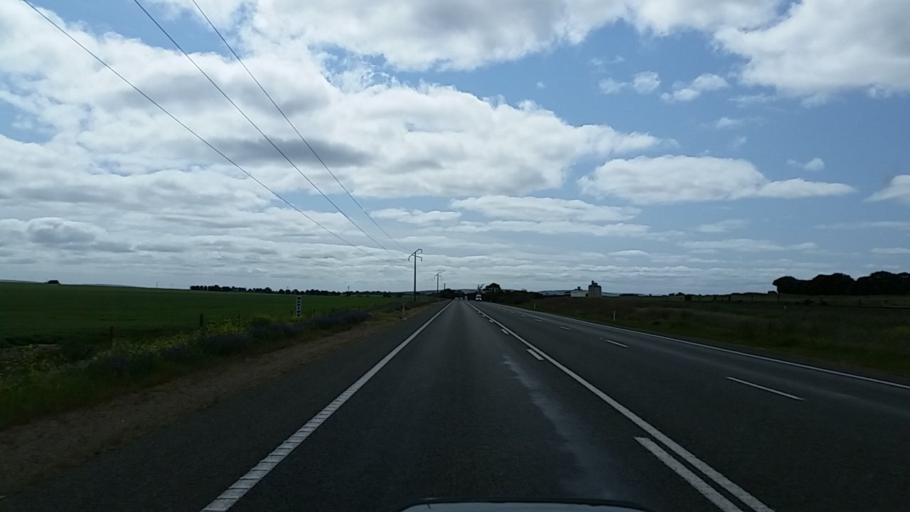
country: AU
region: South Australia
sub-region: Port Pirie City and Dists
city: Crystal Brook
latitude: -33.5592
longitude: 138.2234
